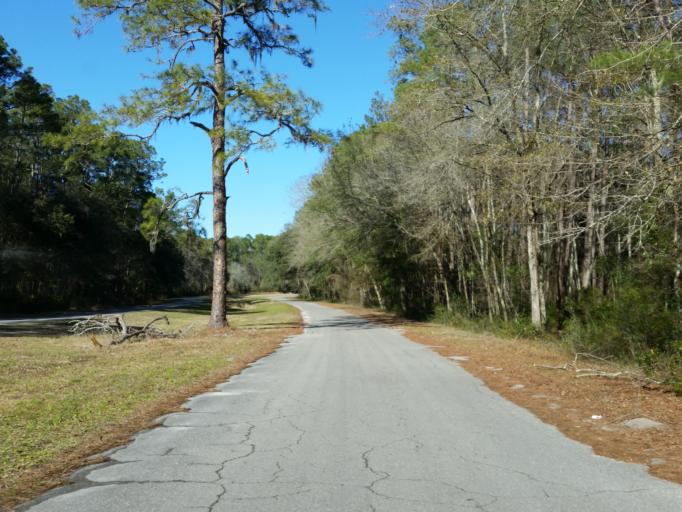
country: US
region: Florida
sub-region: Suwannee County
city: Wellborn
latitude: 30.3373
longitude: -82.7691
